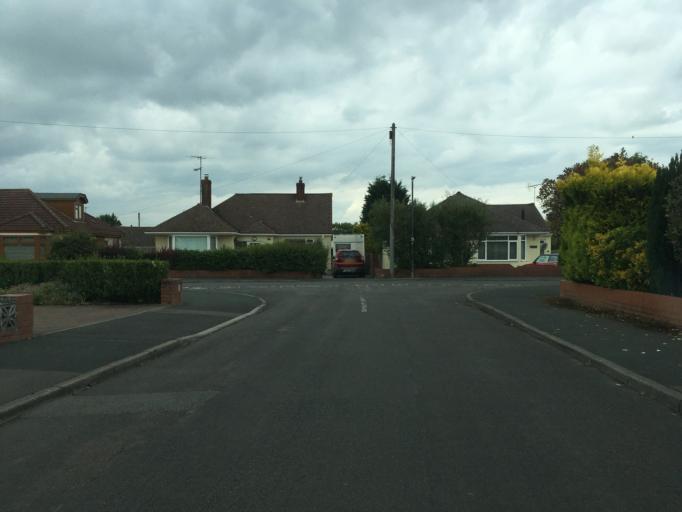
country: GB
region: England
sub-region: South Gloucestershire
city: Winterbourne
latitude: 51.5353
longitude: -2.4911
